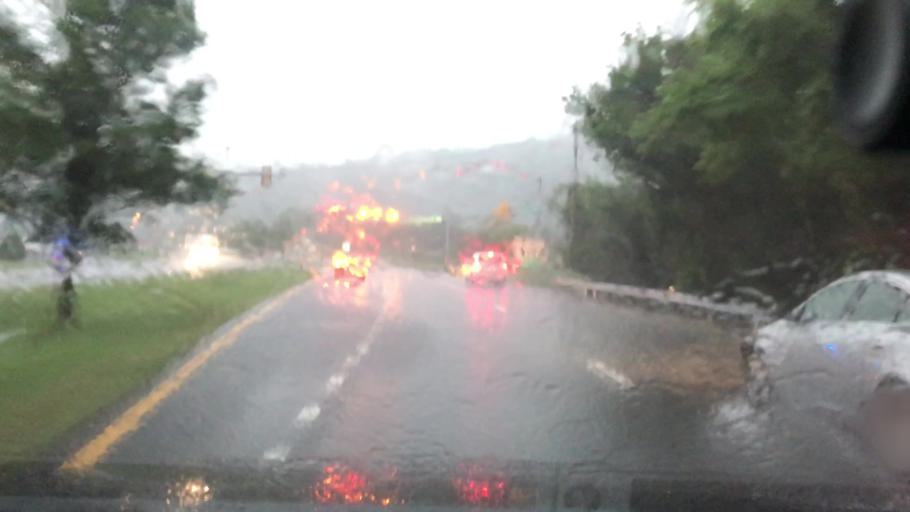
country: US
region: Virginia
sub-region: Giles County
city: Narrows
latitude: 37.3349
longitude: -80.8061
